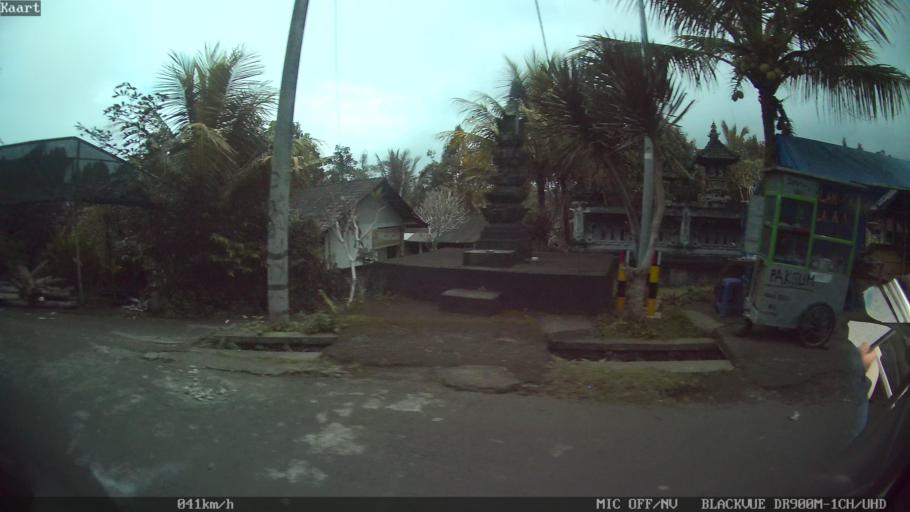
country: ID
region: Bali
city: Banjar Bias
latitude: -8.3737
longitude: 115.4363
